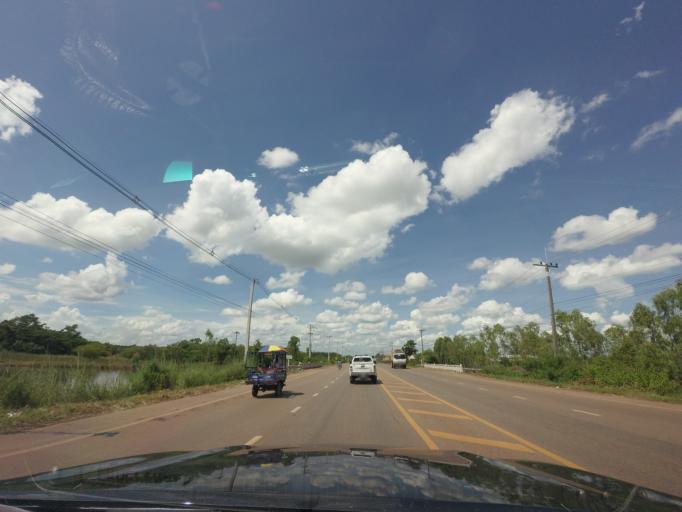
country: TH
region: Changwat Udon Thani
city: Ban Dung
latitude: 17.7191
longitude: 103.2501
